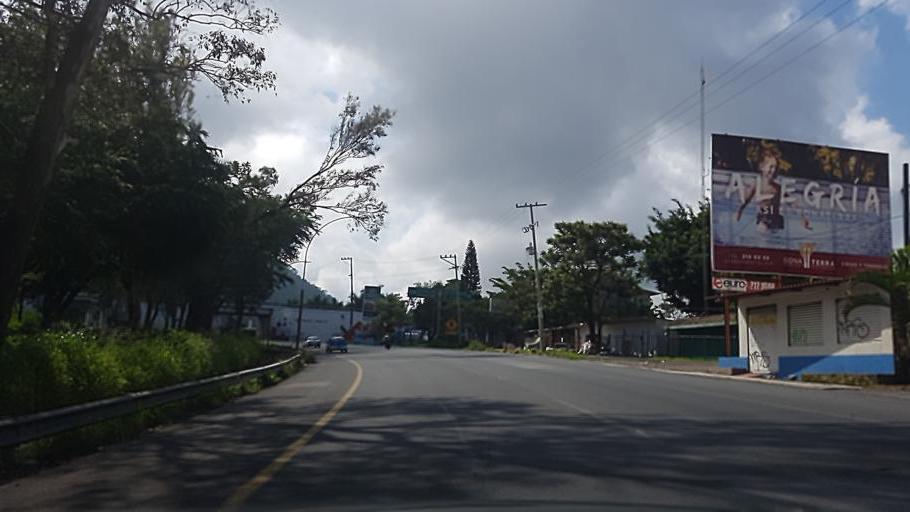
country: MX
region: Nayarit
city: Tepic
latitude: 21.4997
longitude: -104.9101
